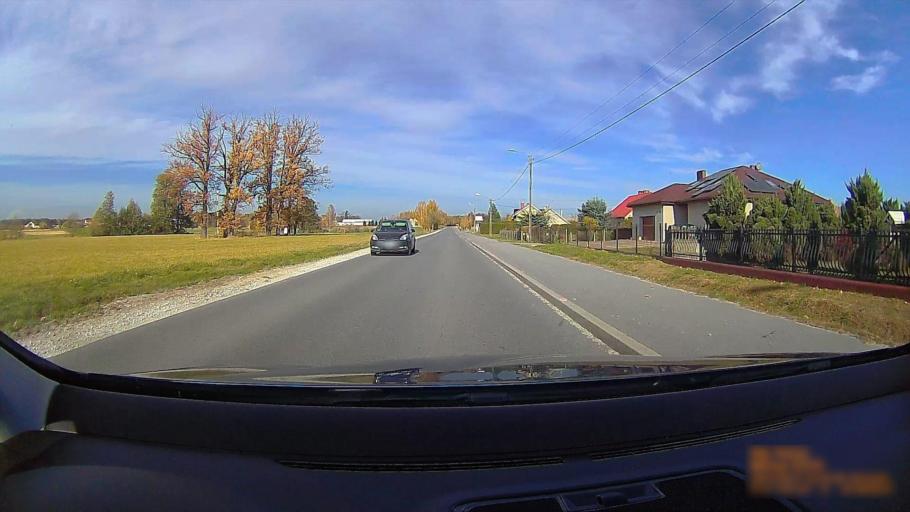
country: PL
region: Greater Poland Voivodeship
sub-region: Powiat kepinski
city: Kepno
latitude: 51.3184
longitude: 18.0139
